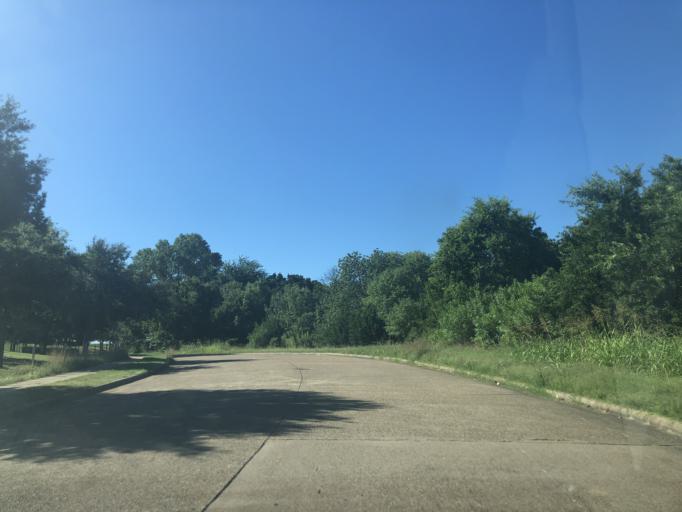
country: US
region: Texas
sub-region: Dallas County
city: Duncanville
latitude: 32.6664
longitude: -96.9304
